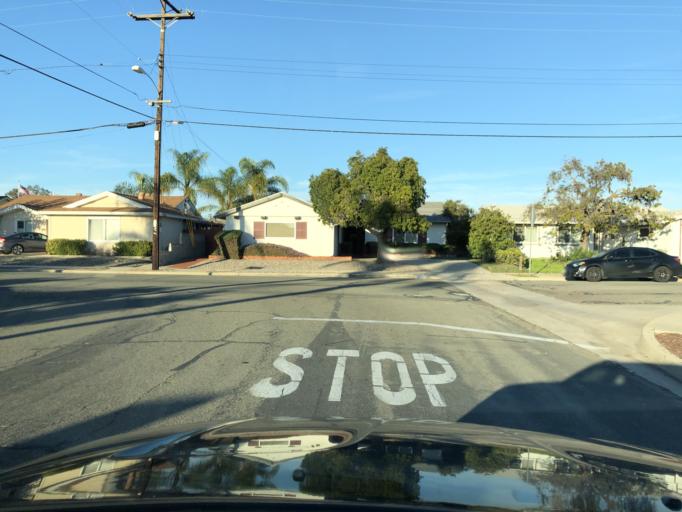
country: US
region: California
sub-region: San Diego County
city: La Jolla
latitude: 32.8213
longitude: -117.1948
